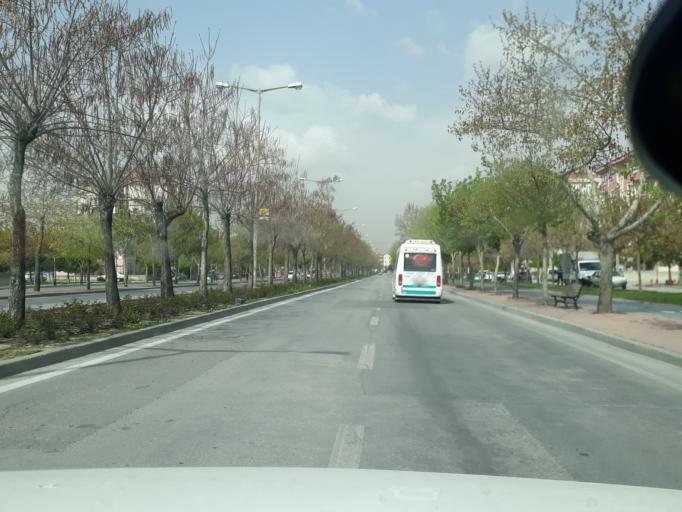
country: TR
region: Konya
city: Selcuklu
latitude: 37.9372
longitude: 32.4985
